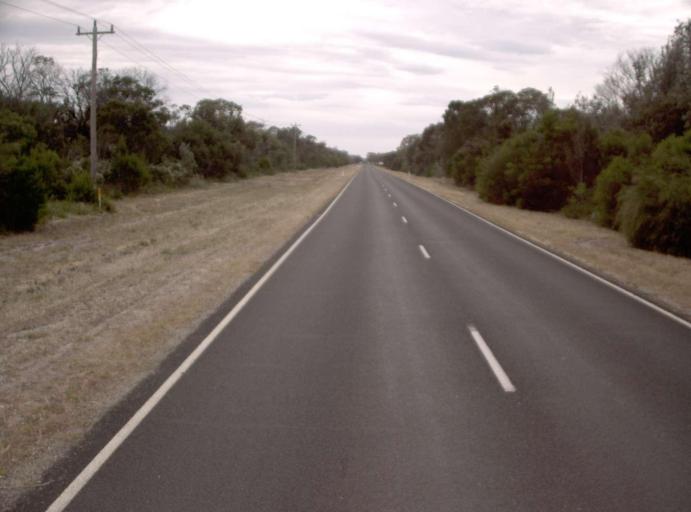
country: AU
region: Victoria
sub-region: East Gippsland
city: Bairnsdale
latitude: -38.0651
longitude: 147.5571
